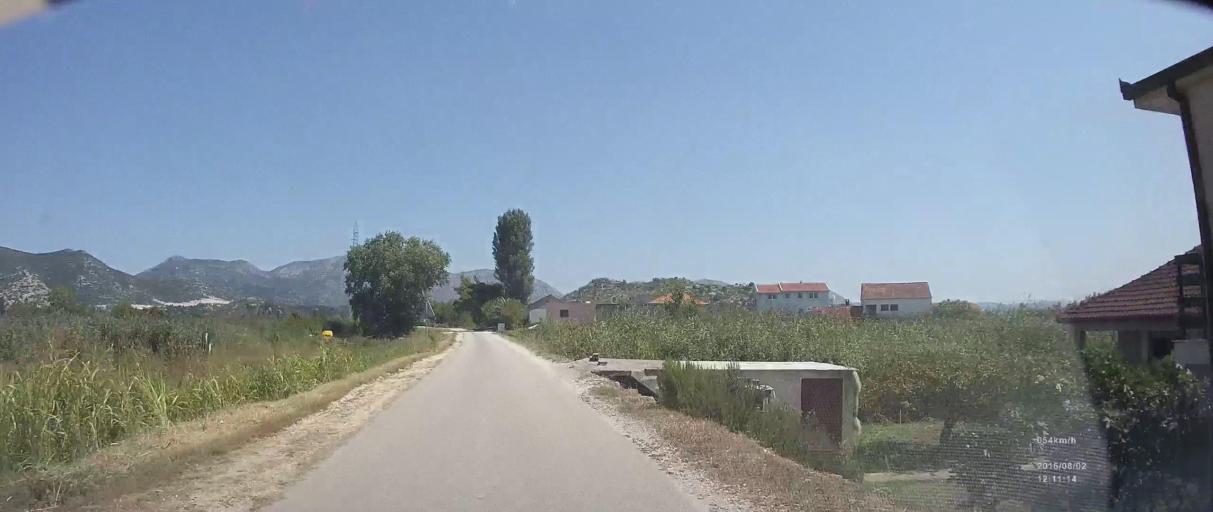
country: HR
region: Dubrovacko-Neretvanska
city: Komin
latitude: 43.0273
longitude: 17.4620
